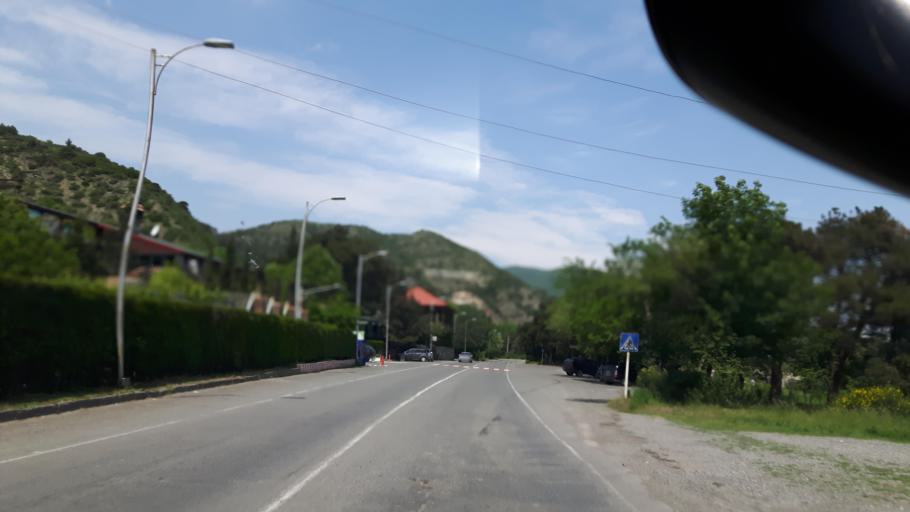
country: GE
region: Mtskheta-Mtianeti
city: Mtskheta
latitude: 41.8279
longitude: 44.7260
